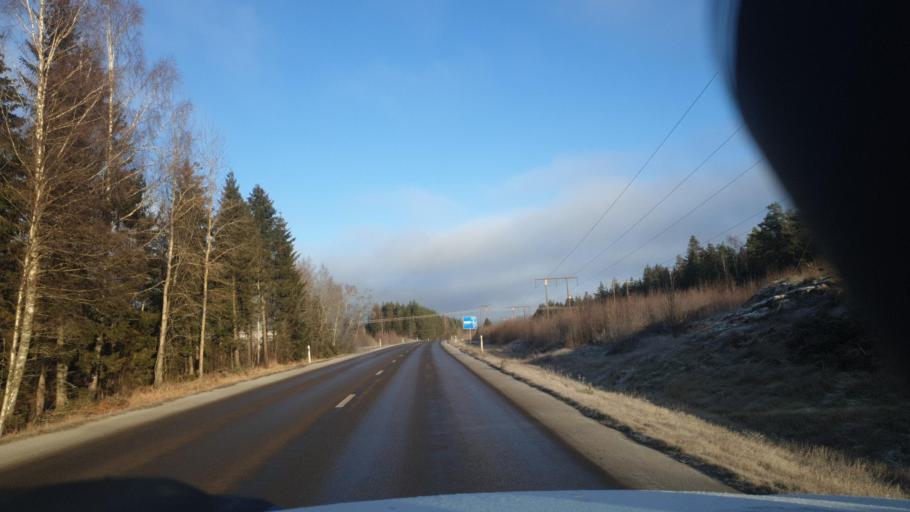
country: SE
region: Vaermland
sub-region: Karlstads Kommun
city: Edsvalla
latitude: 59.4136
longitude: 13.1847
